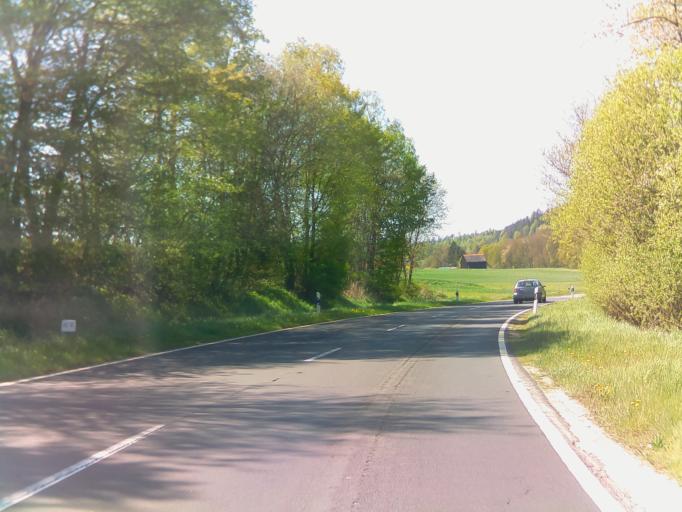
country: DE
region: Hesse
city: Grebenau
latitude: 50.7759
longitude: 9.4913
